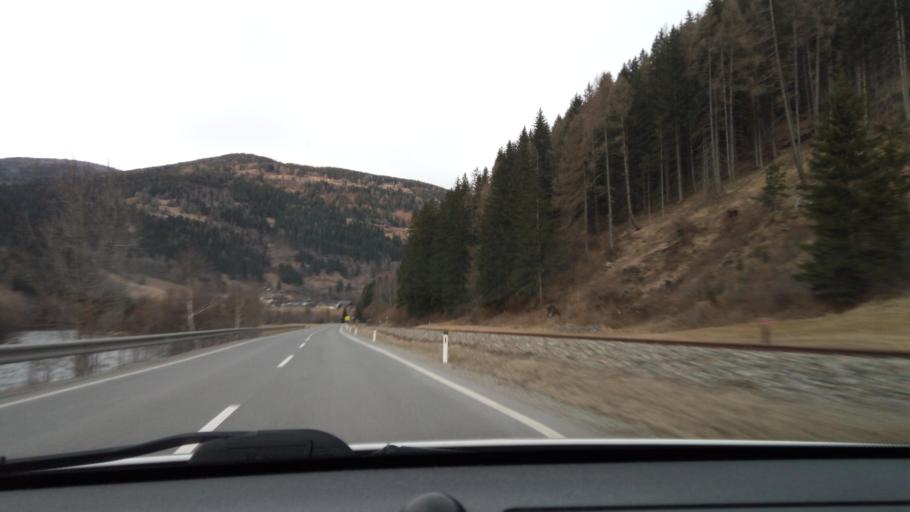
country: AT
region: Styria
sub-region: Politischer Bezirk Murau
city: Stadl an der Mur
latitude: 47.0800
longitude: 13.9306
